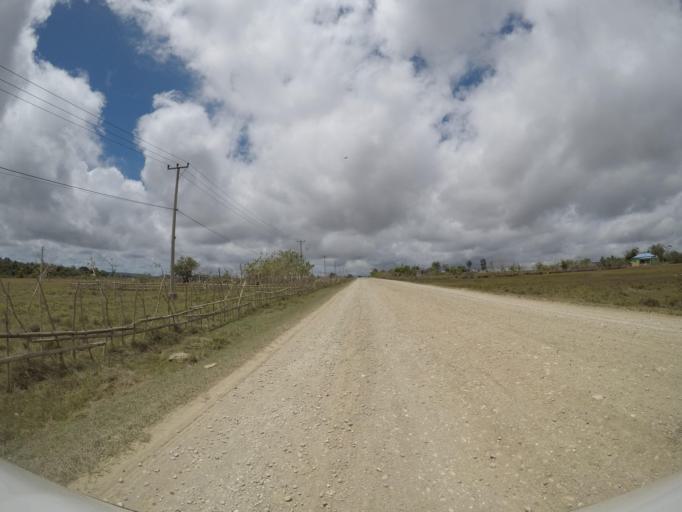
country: TL
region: Lautem
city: Lospalos
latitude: -8.4405
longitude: 126.9871
